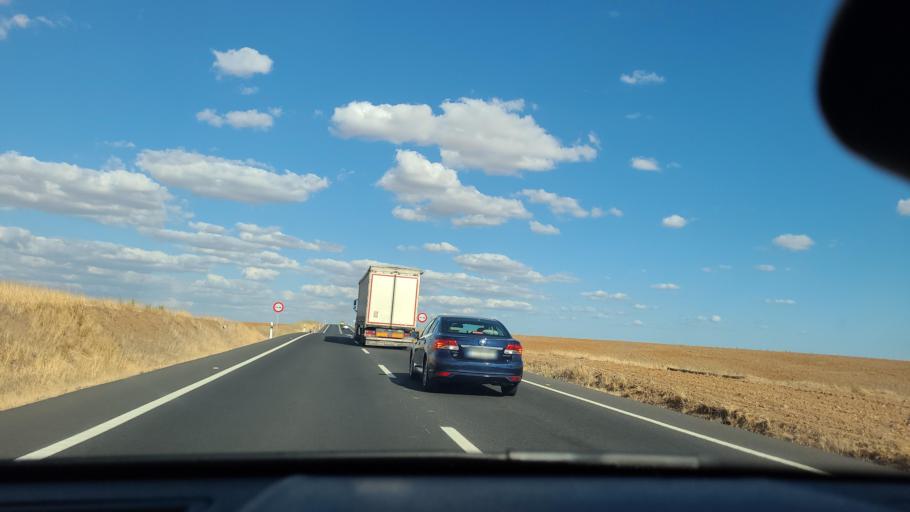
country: ES
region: Extremadura
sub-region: Provincia de Badajoz
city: Azuaga
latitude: 38.2648
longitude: -5.7476
